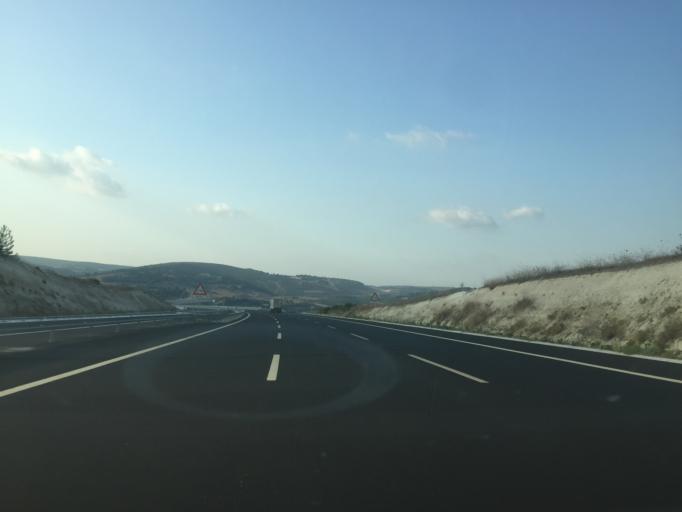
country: TR
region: Balikesir
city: Ertugrul
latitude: 39.5681
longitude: 27.7024
